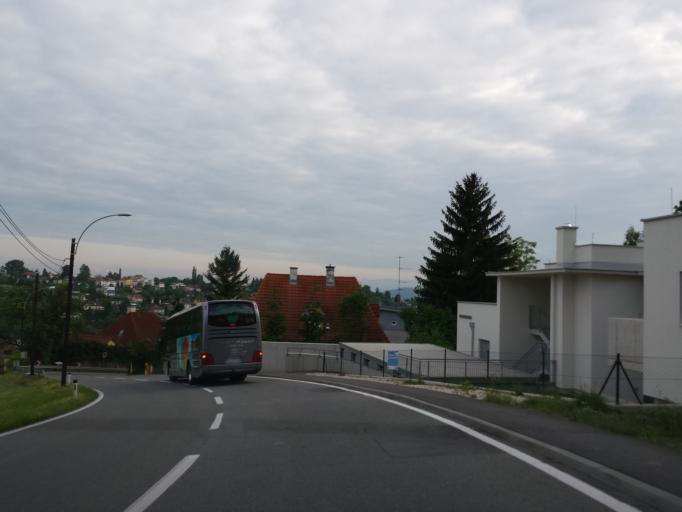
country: AT
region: Styria
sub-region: Graz Stadt
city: Graz
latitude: 47.0816
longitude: 15.4753
